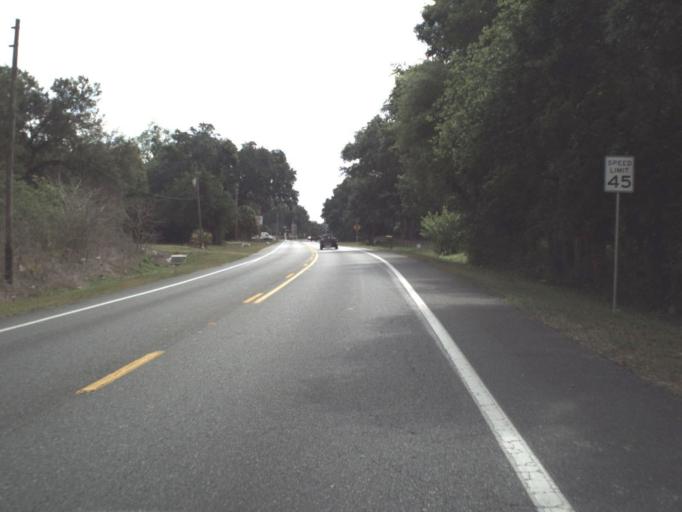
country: US
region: Florida
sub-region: Marion County
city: Ocala
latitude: 29.2592
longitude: -82.1188
